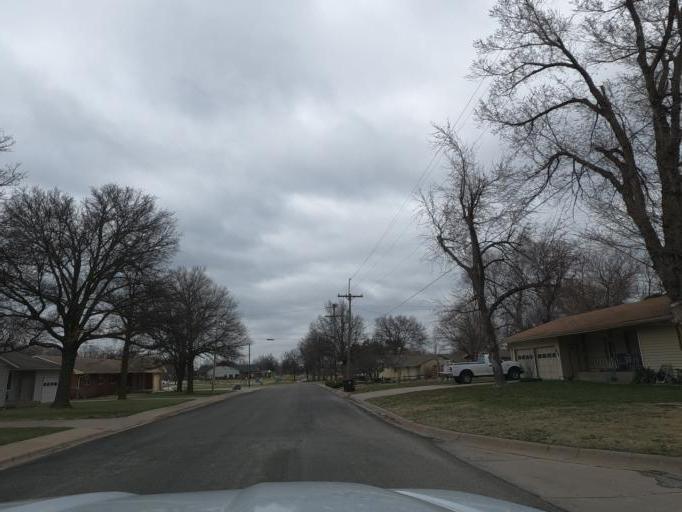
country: US
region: Kansas
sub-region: McPherson County
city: Inman
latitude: 38.2291
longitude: -97.7705
